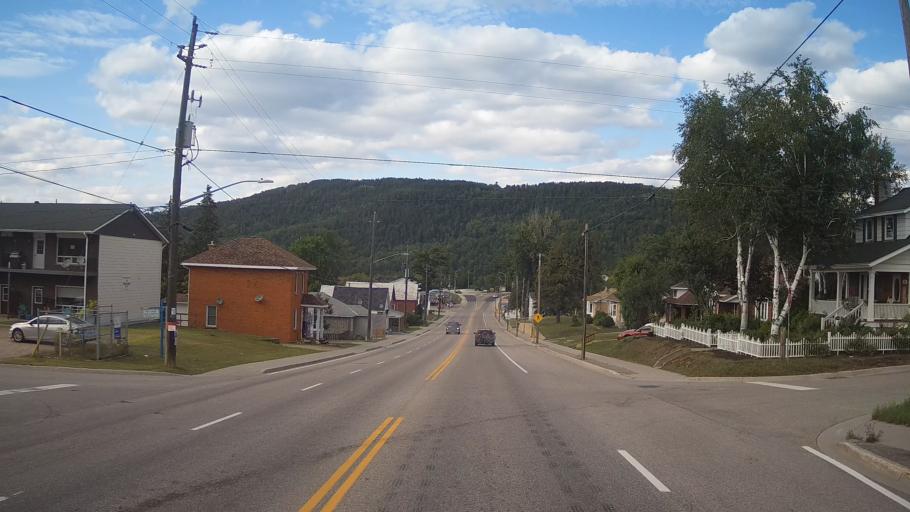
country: CA
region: Ontario
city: Mattawa
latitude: 46.3140
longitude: -78.7037
